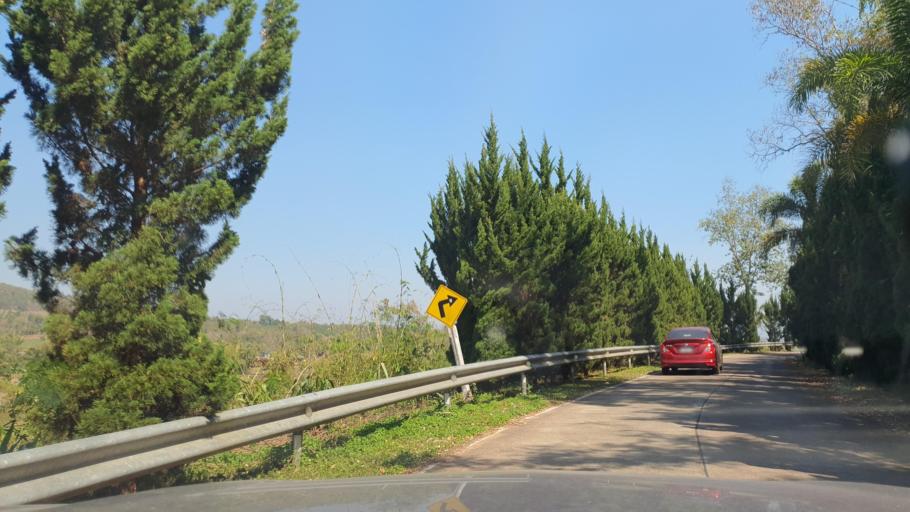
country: TH
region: Lampang
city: Wang Nuea
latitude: 19.1852
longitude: 99.4957
